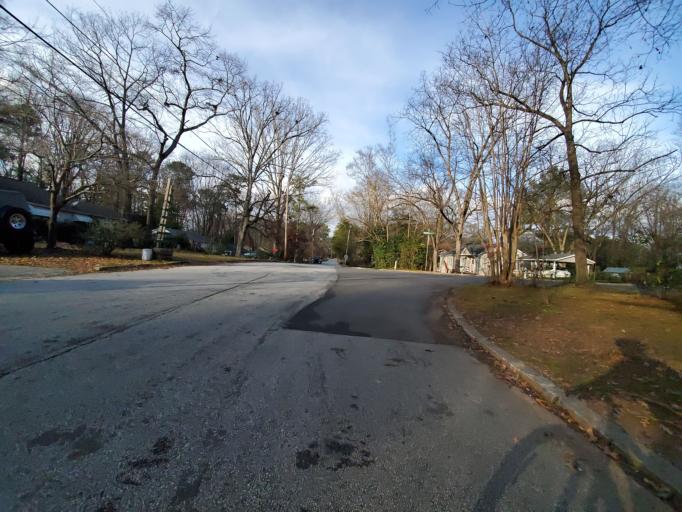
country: US
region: Georgia
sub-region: DeKalb County
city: North Decatur
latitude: 33.7982
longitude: -84.2971
